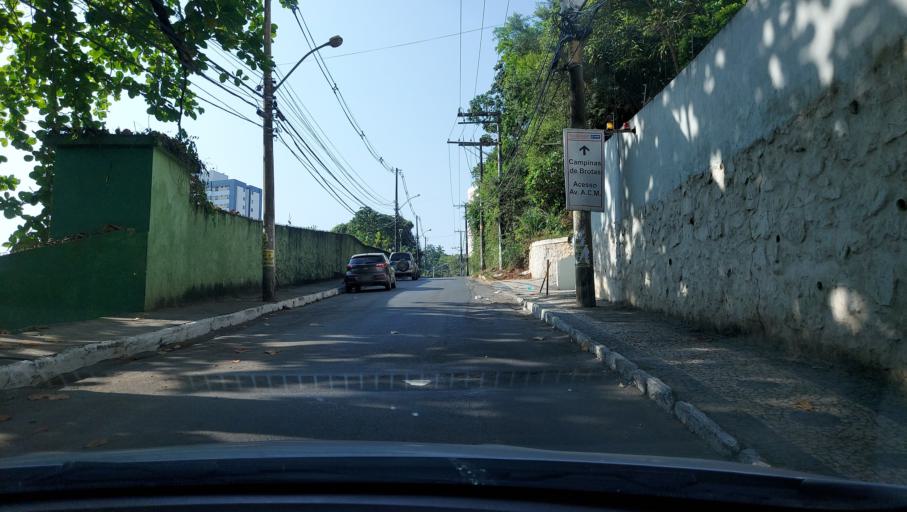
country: BR
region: Bahia
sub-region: Salvador
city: Salvador
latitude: -12.9876
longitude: -38.4693
